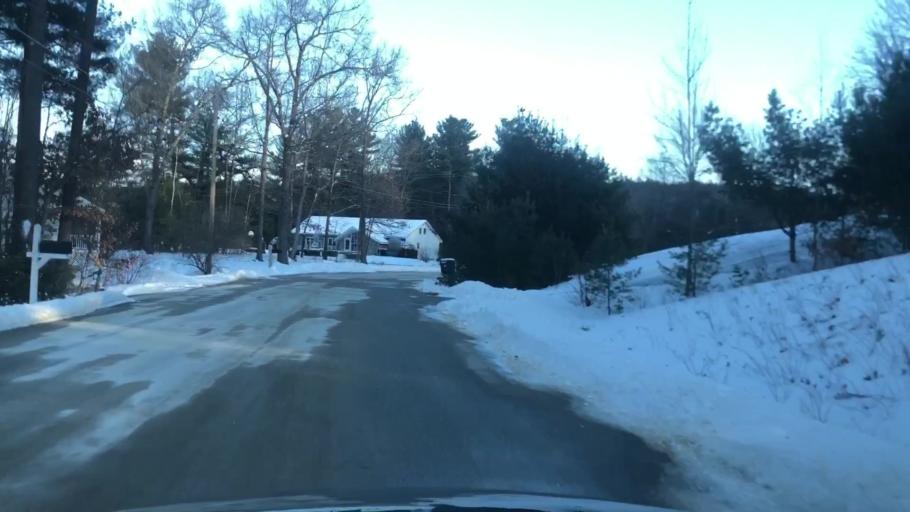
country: US
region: New Hampshire
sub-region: Hillsborough County
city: Milford
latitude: 42.8154
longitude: -71.6690
